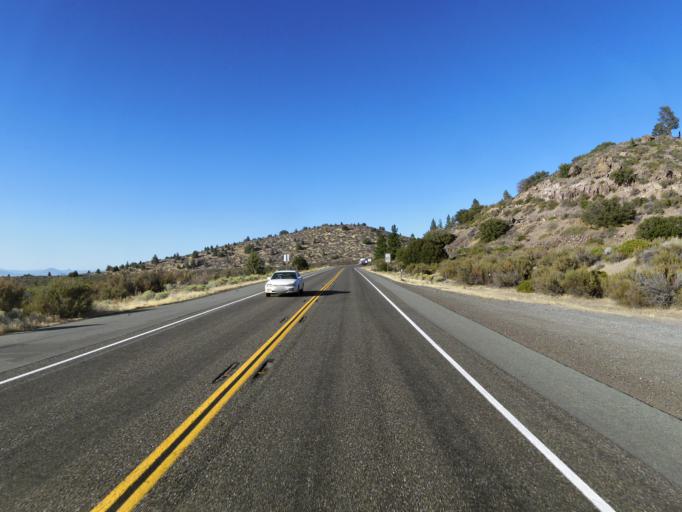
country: US
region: California
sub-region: Siskiyou County
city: Weed
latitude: 41.4743
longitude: -122.3510
